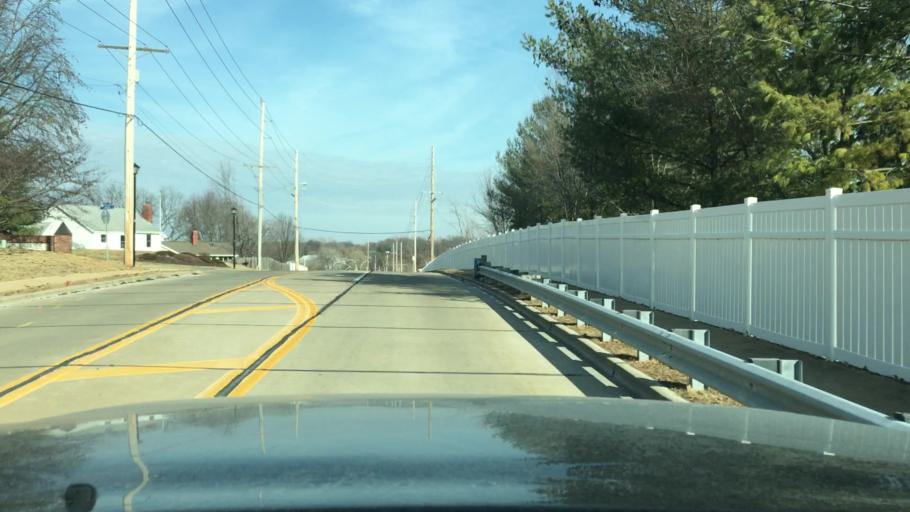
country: US
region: Missouri
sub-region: Saint Charles County
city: Saint Peters
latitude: 38.8030
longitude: -90.5585
